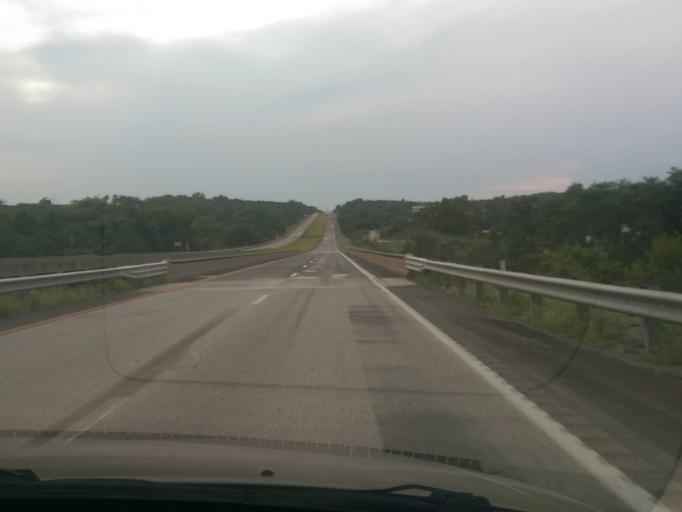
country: US
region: Missouri
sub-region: Andrew County
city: Savannah
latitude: 39.9012
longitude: -94.8805
